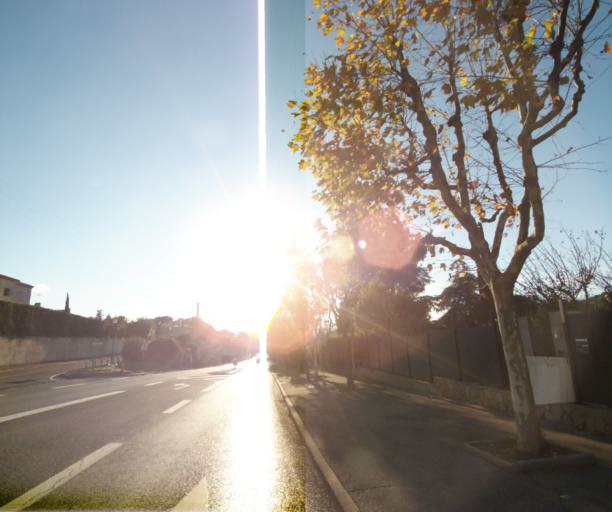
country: FR
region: Provence-Alpes-Cote d'Azur
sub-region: Departement des Bouches-du-Rhone
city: Carnoux-en-Provence
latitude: 43.2512
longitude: 5.5562
